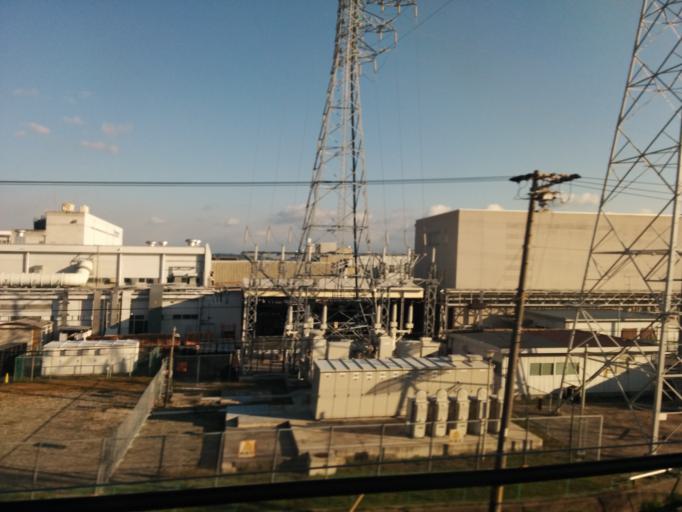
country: JP
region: Shizuoka
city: Kosai-shi
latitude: 34.7134
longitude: 137.4910
